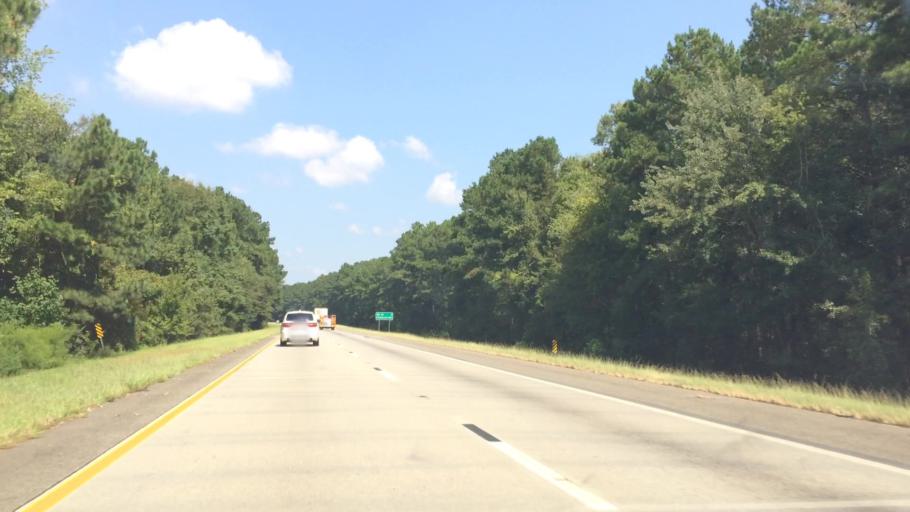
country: US
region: South Carolina
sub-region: Colleton County
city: Walterboro
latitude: 33.0156
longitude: -80.6662
